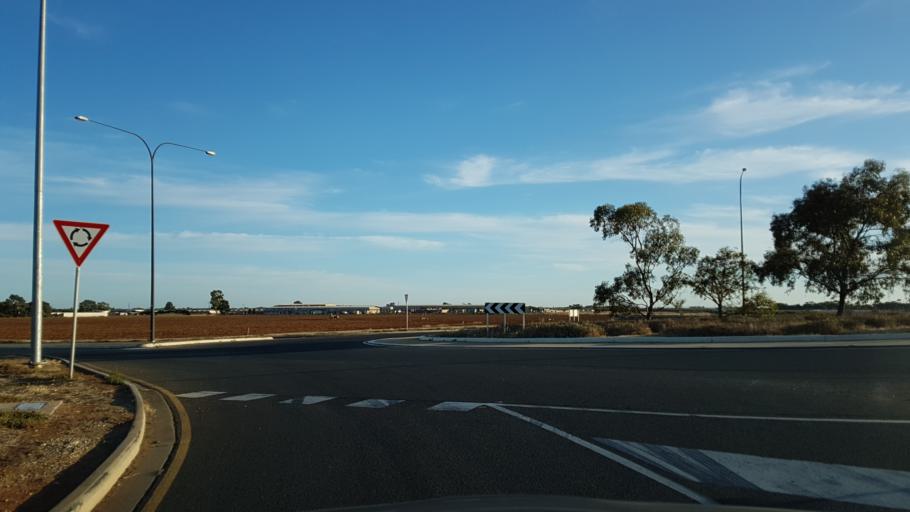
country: AU
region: South Australia
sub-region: Playford
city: Virginia
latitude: -34.6840
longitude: 138.5981
